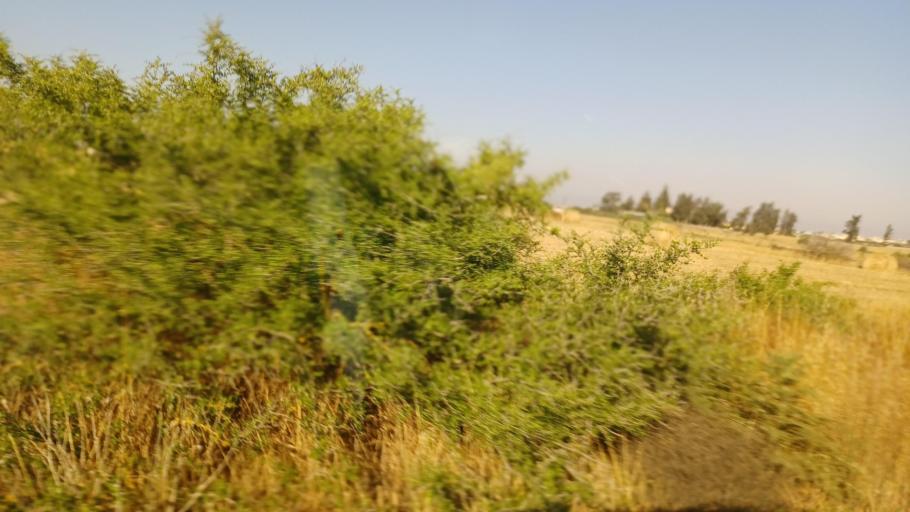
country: CY
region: Ammochostos
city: Frenaros
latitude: 35.0729
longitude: 33.8996
